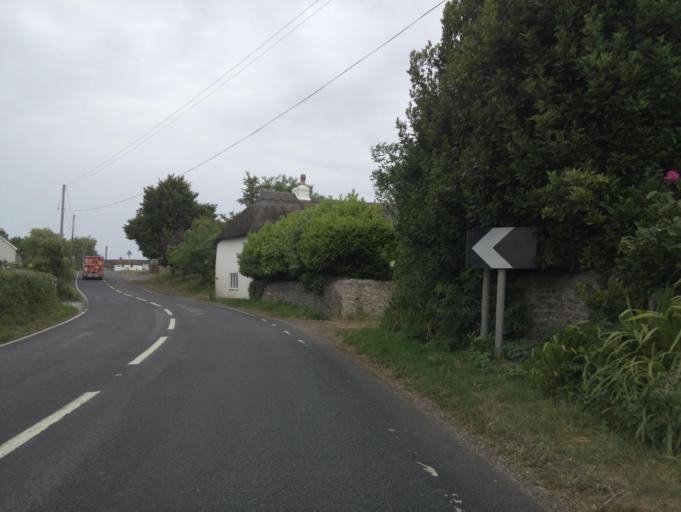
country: GB
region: England
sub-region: Devon
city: Colyton
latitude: 50.7456
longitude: -3.0339
